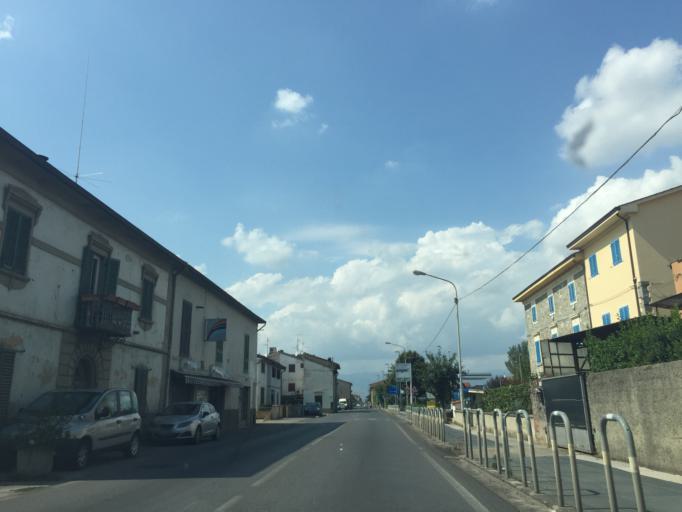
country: IT
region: Tuscany
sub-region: Provincia di Pistoia
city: Barba
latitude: 43.8798
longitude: 10.9748
